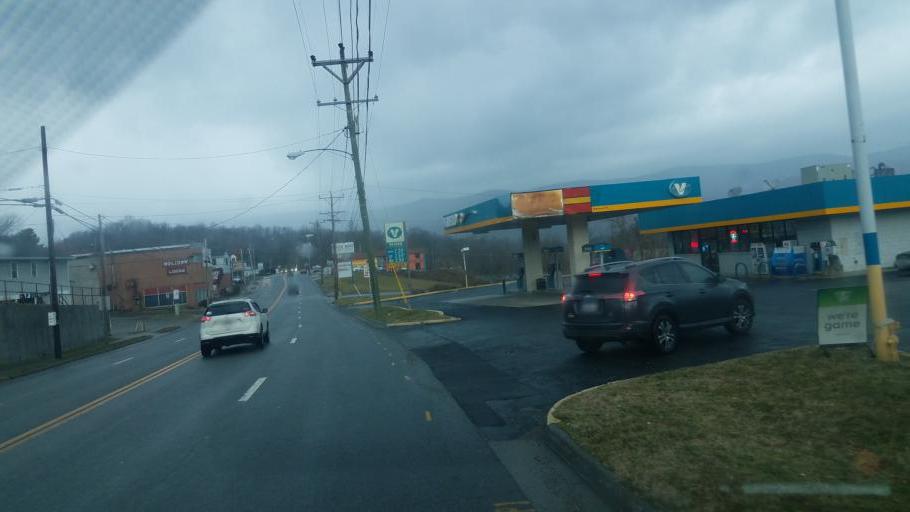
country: US
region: Virginia
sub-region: Giles County
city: Pearisburg
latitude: 37.3287
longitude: -80.7364
